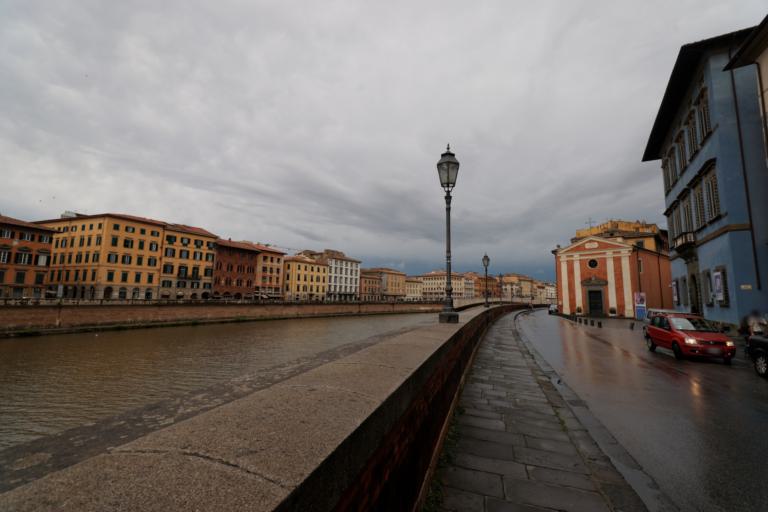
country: IT
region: Tuscany
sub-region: Province of Pisa
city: Pisa
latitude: 43.7158
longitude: 10.3991
